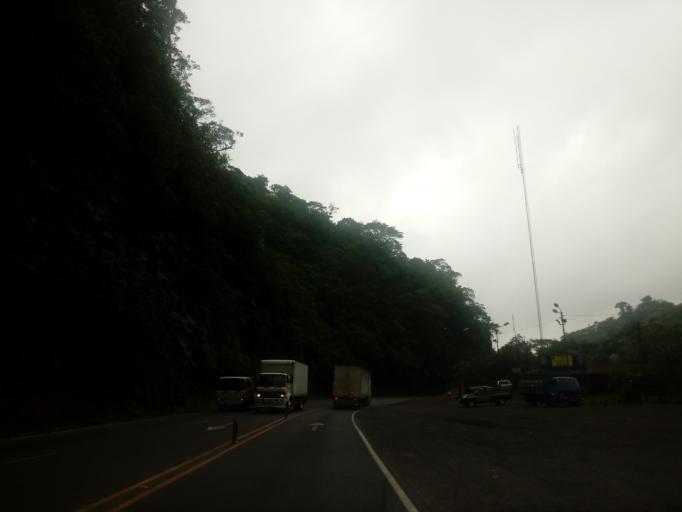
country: CR
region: Heredia
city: Angeles
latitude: 10.0576
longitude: -84.0129
